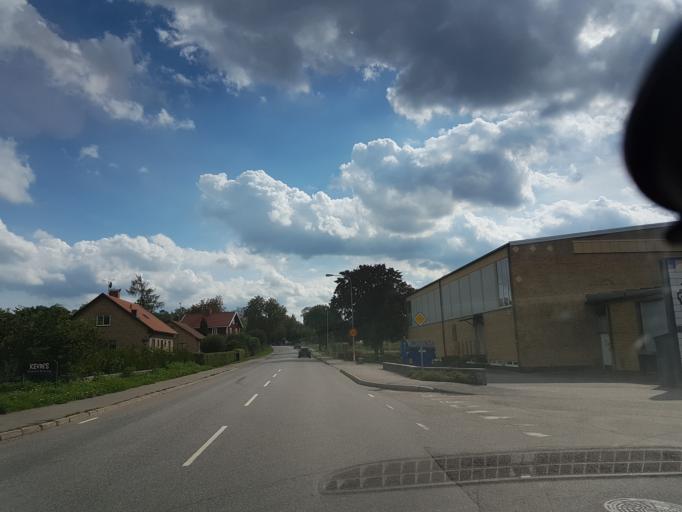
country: SE
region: OEstergoetland
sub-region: Linkopings Kommun
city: Vikingstad
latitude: 58.3814
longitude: 15.4367
